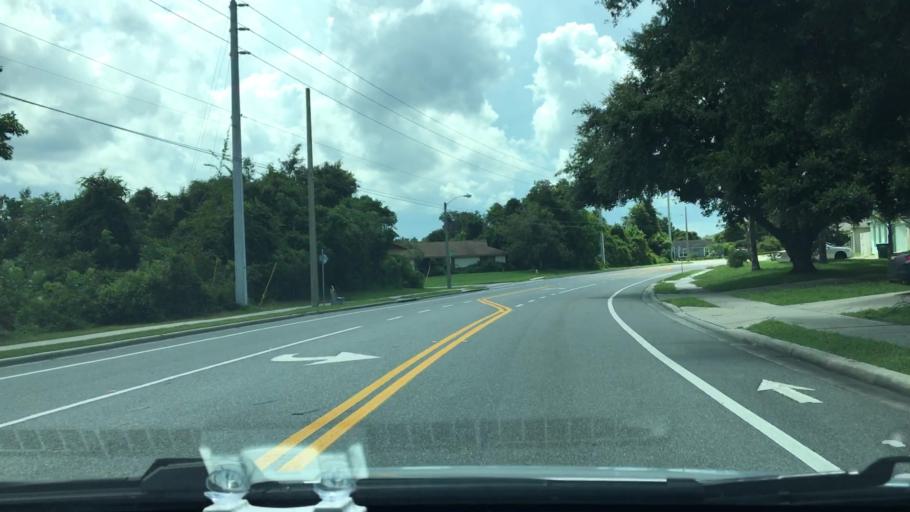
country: US
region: Florida
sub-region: Volusia County
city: Deltona
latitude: 28.8782
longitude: -81.2015
